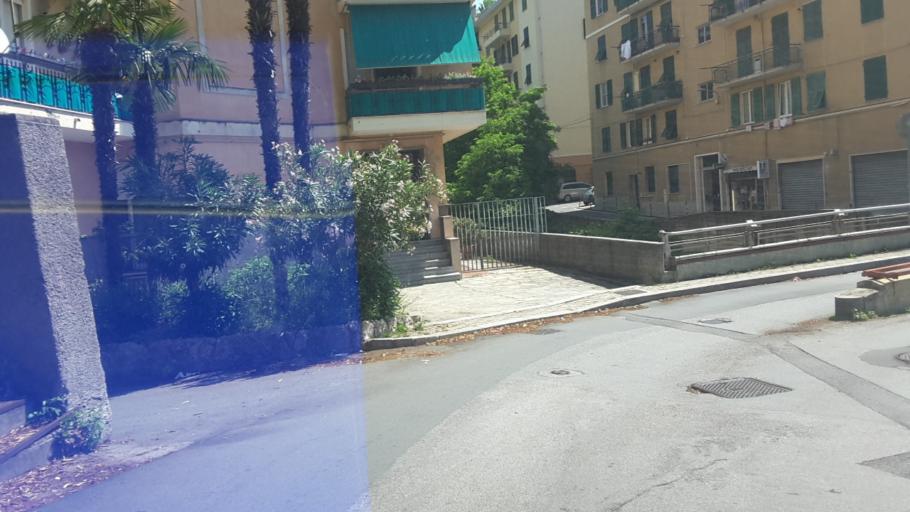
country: IT
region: Liguria
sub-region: Provincia di Genova
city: Mele
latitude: 44.4300
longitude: 8.7892
